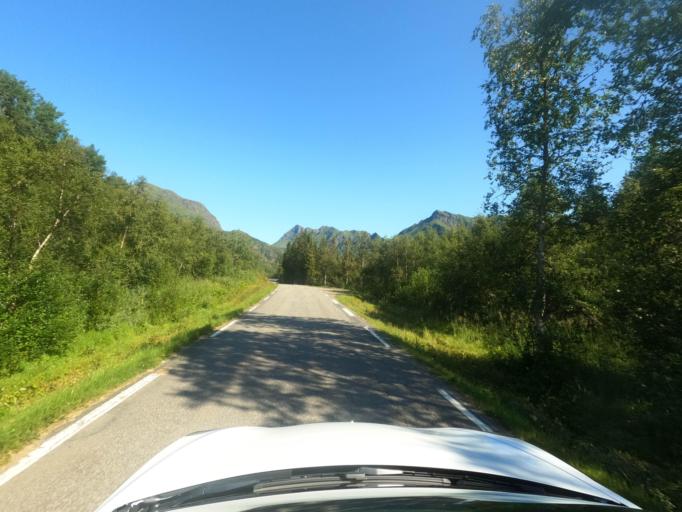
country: NO
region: Nordland
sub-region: Hadsel
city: Stokmarknes
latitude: 68.3044
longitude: 15.0507
